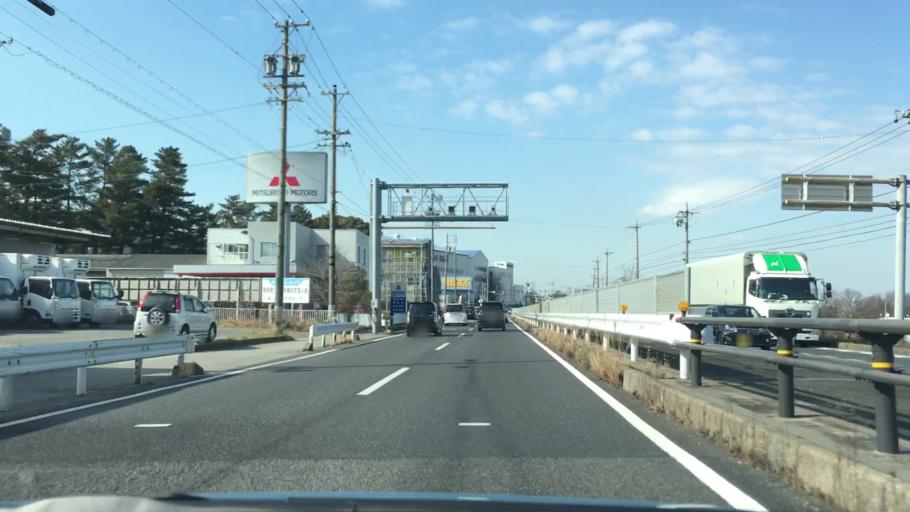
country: JP
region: Aichi
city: Okazaki
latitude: 34.9171
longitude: 137.2117
